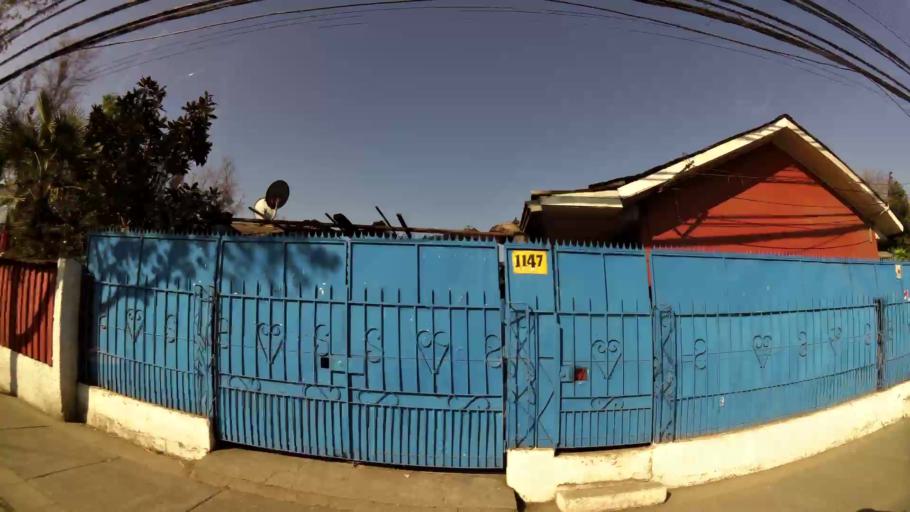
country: CL
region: Santiago Metropolitan
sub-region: Provincia de Santiago
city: Villa Presidente Frei, Nunoa, Santiago, Chile
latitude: -33.3583
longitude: -70.5065
